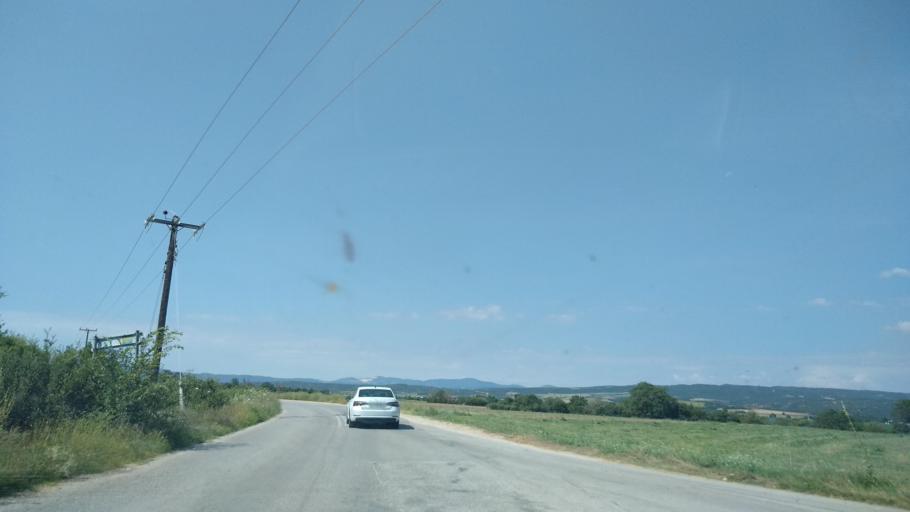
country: GR
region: Central Macedonia
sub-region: Nomos Thessalonikis
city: Nea Apollonia
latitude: 40.6145
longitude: 23.4607
